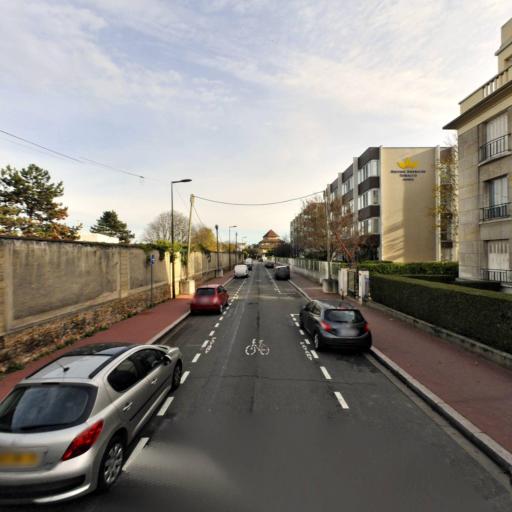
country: FR
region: Ile-de-France
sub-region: Departement des Hauts-de-Seine
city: Suresnes
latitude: 48.8479
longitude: 2.2281
